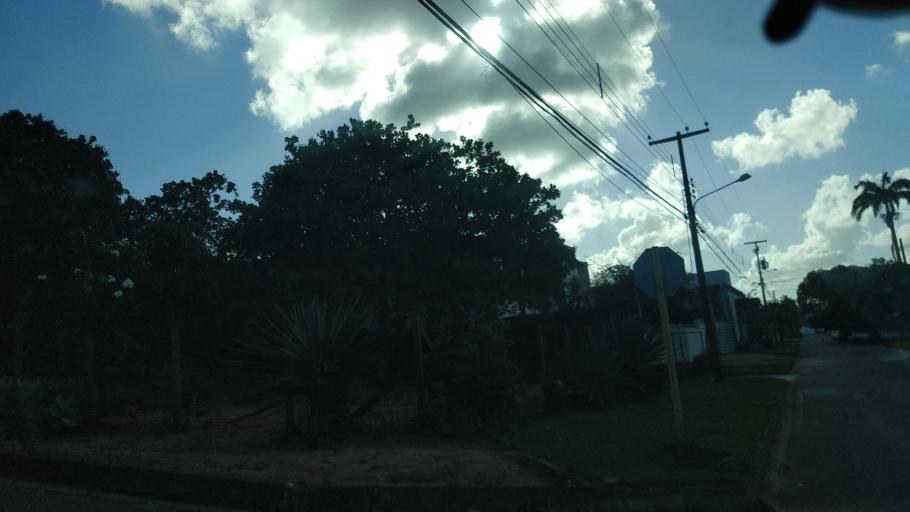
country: BR
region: Rio Grande do Norte
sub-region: Natal
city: Natal
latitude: -5.8465
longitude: -35.2035
